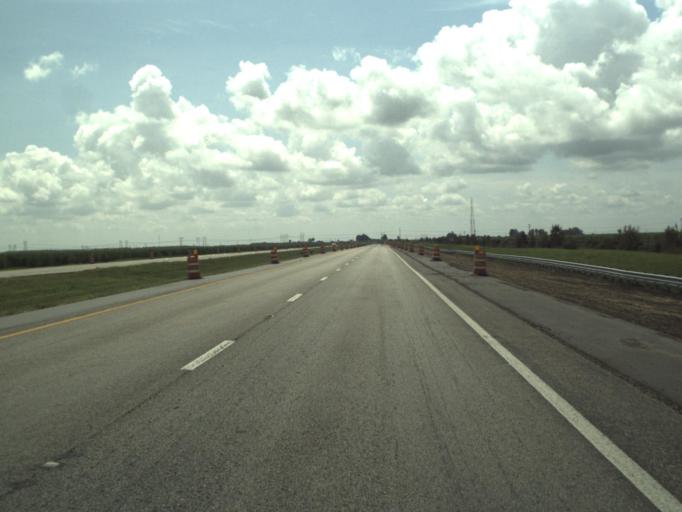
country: US
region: Florida
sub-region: Palm Beach County
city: Loxahatchee Groves
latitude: 26.7029
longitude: -80.4102
